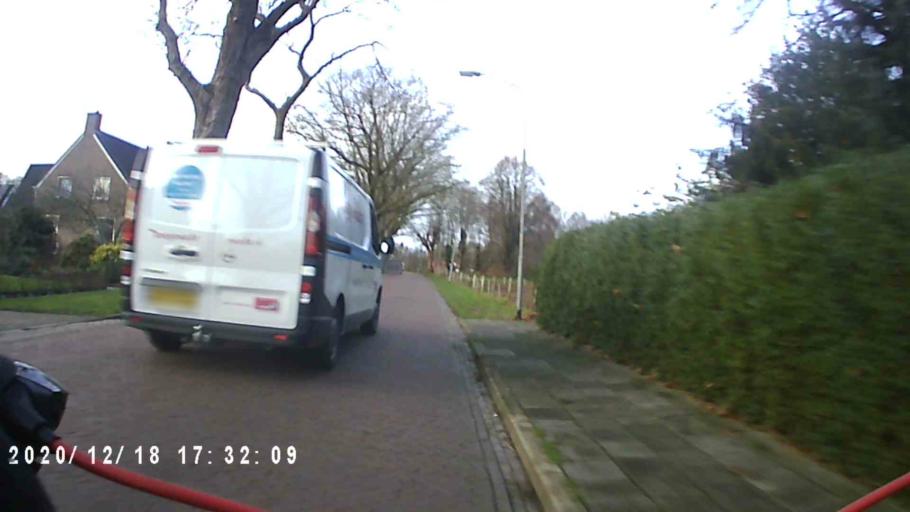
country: NL
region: Drenthe
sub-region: Gemeente Tynaarlo
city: Vries
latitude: 53.0803
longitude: 6.5753
